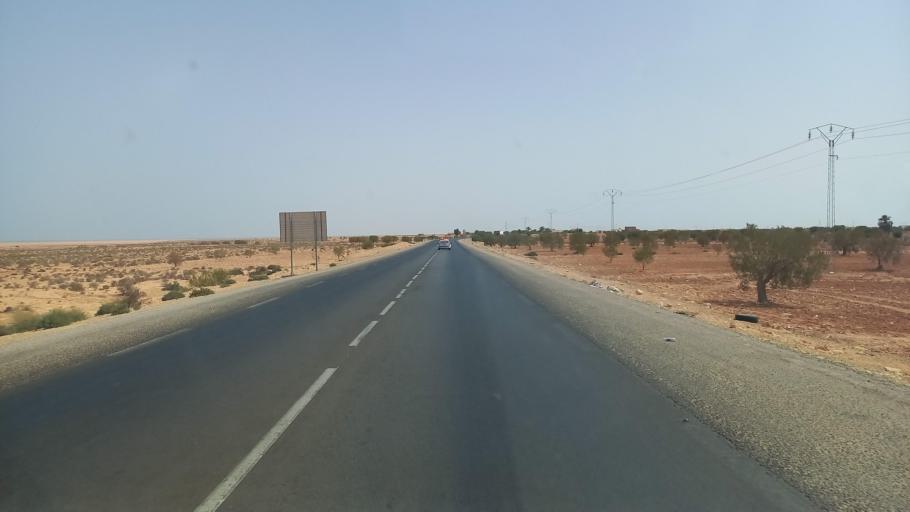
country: TN
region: Madanin
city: Medenine
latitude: 33.3867
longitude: 10.7047
